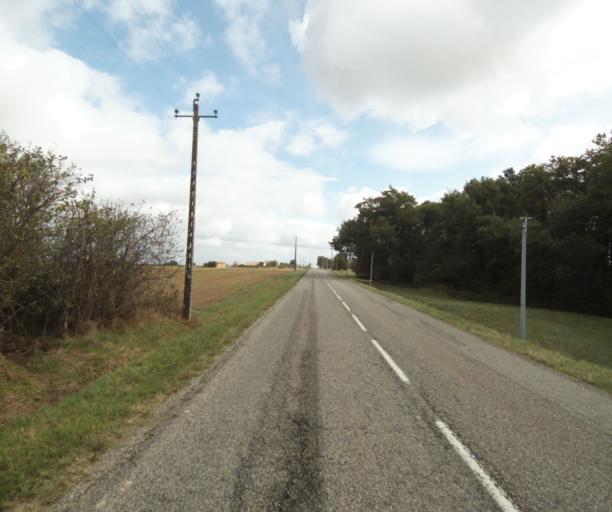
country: FR
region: Midi-Pyrenees
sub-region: Departement du Tarn-et-Garonne
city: Beaumont-de-Lomagne
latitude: 43.8651
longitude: 1.0743
